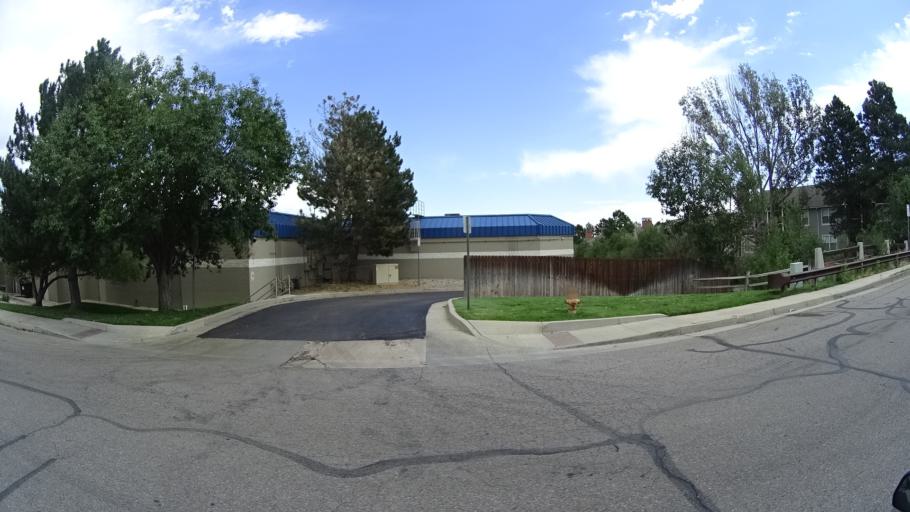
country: US
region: Colorado
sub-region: El Paso County
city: Stratmoor
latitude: 38.7746
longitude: -104.8168
